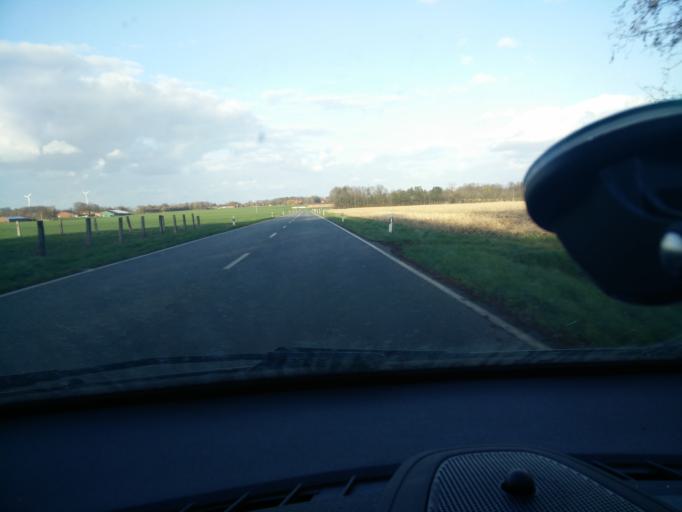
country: DE
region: North Rhine-Westphalia
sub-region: Regierungsbezirk Munster
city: Raesfeld
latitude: 51.7618
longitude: 6.7975
